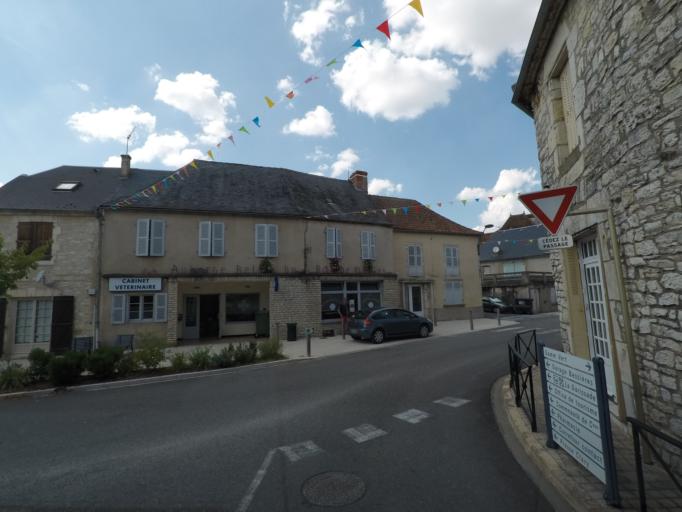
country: FR
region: Midi-Pyrenees
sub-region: Departement du Lot
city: Le Vigan
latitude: 44.6467
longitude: 1.5686
